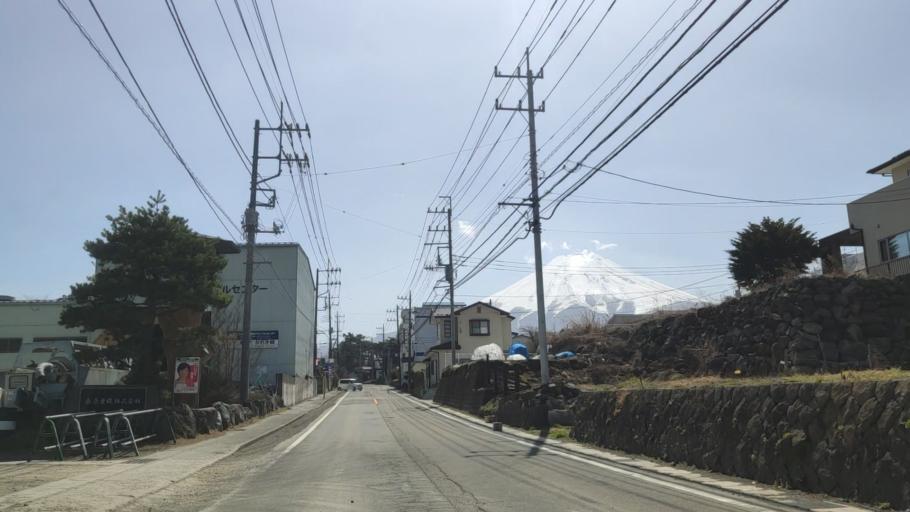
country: JP
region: Yamanashi
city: Fujikawaguchiko
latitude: 35.4716
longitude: 138.8136
